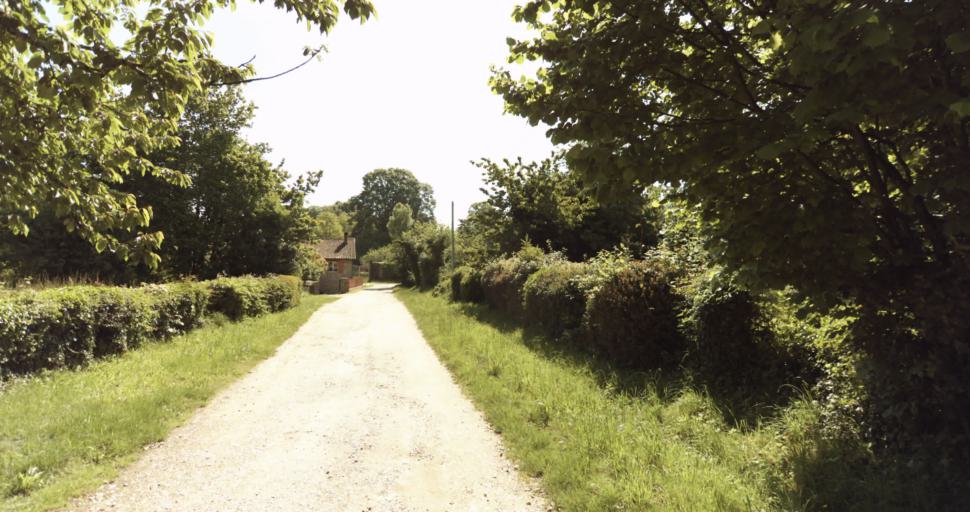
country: FR
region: Limousin
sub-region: Departement de la Haute-Vienne
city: Solignac
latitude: 45.7236
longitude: 1.2612
